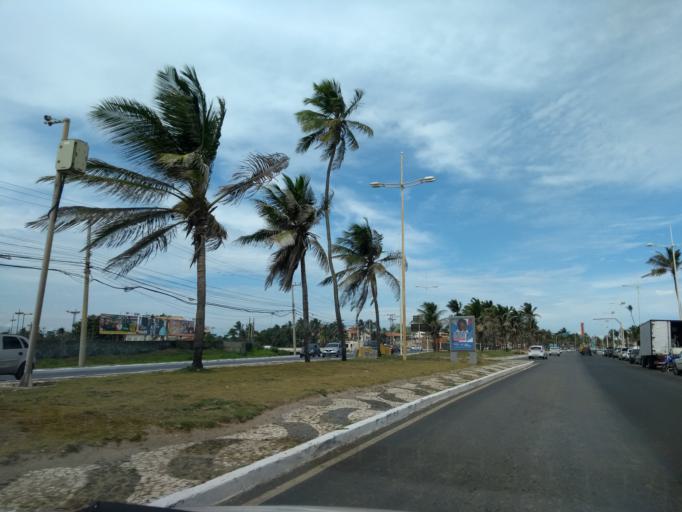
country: BR
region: Bahia
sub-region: Lauro De Freitas
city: Lauro de Freitas
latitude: -12.9555
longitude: -38.3863
